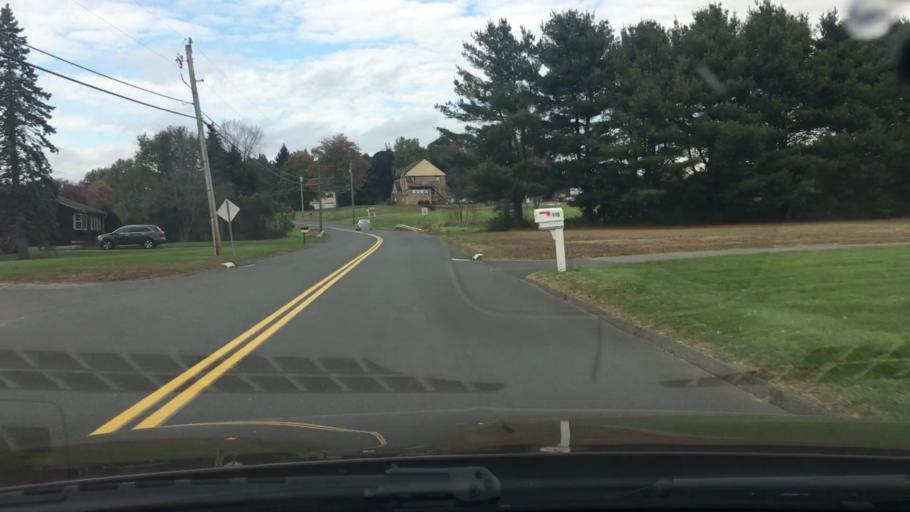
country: US
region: Connecticut
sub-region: Tolland County
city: Ellington
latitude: 41.9187
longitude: -72.4750
